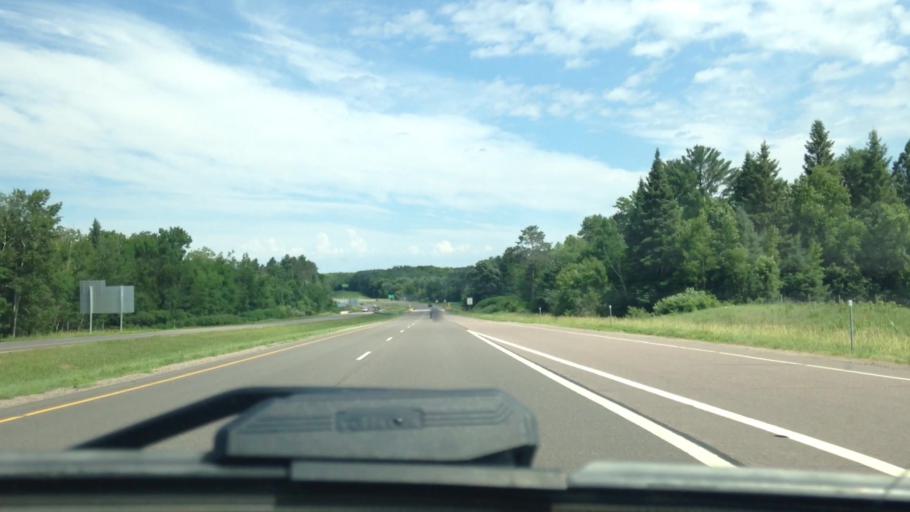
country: US
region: Wisconsin
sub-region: Washburn County
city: Spooner
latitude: 45.8210
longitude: -91.8560
